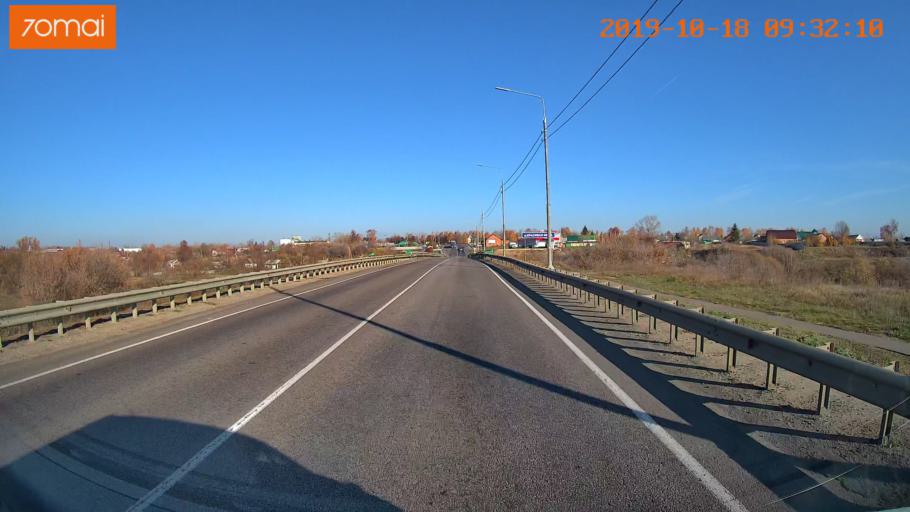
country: RU
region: Tula
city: Yefremov
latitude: 53.1583
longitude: 38.1560
